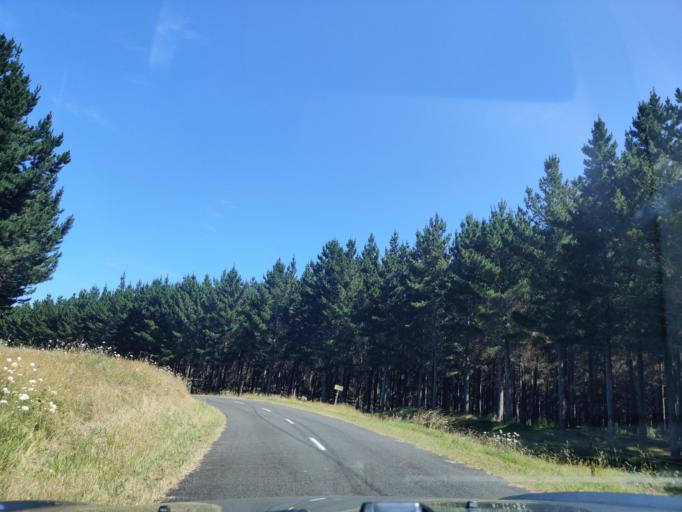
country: NZ
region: Waikato
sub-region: Waikato District
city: Raglan
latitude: -38.0665
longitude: 174.7901
